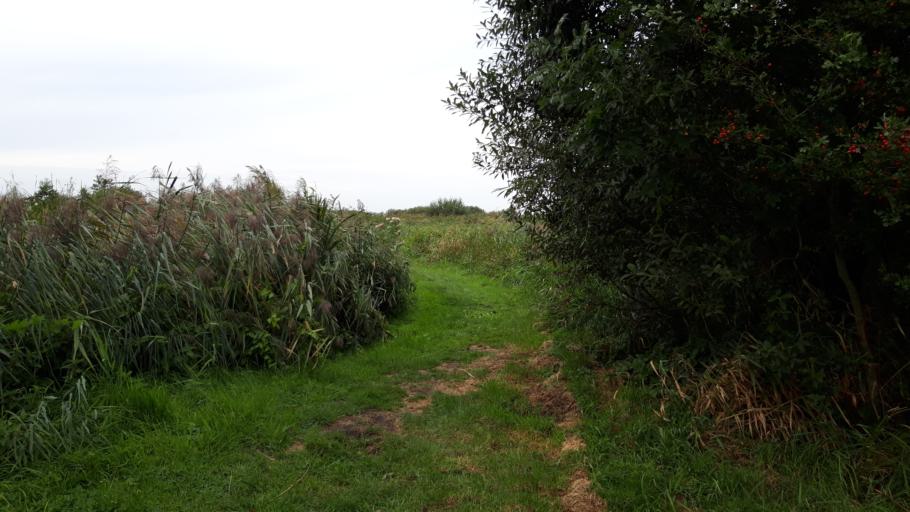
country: NL
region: Friesland
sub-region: Gemeente Boarnsterhim
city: Warten
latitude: 53.1157
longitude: 5.8859
